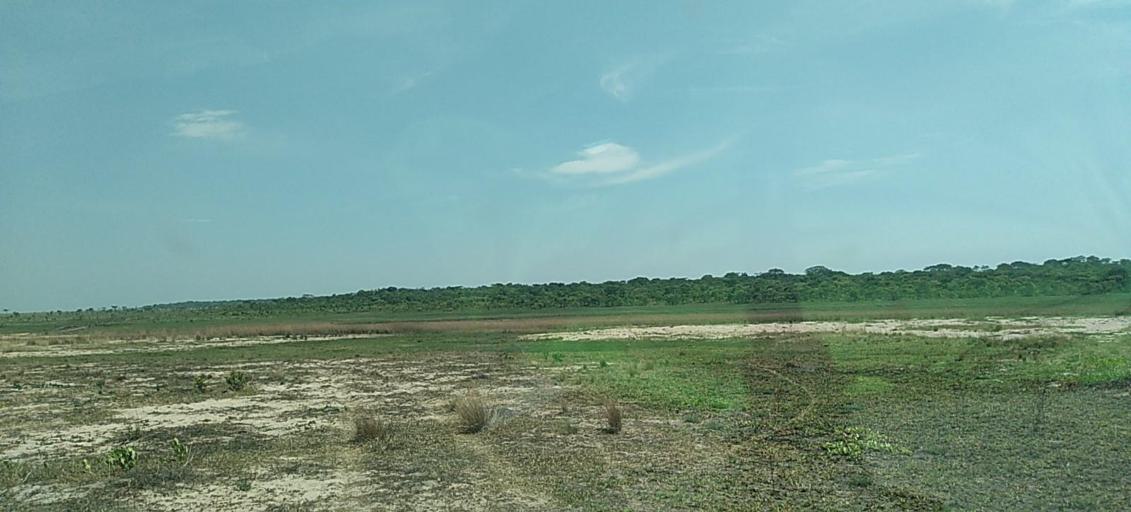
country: ZM
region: North-Western
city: Mwinilunga
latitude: -11.6694
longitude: 25.2059
